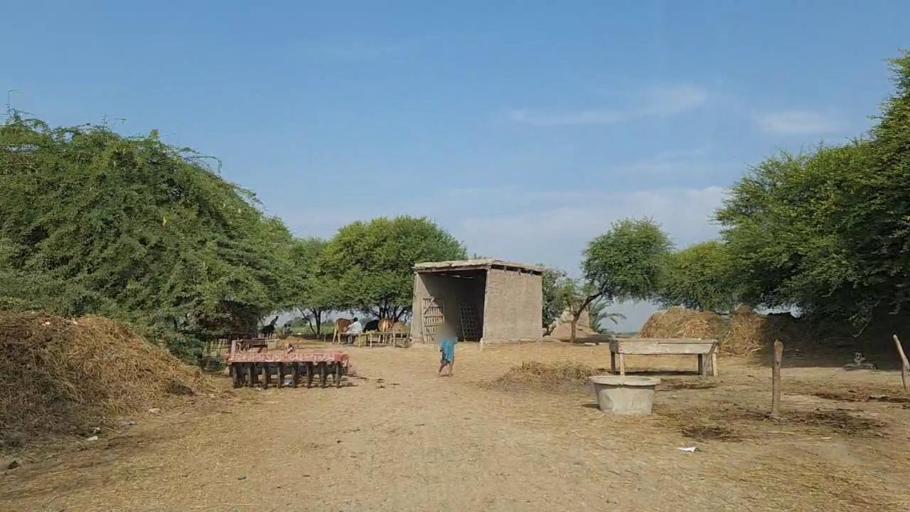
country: PK
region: Sindh
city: Mirpur Batoro
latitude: 24.7194
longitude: 68.2172
